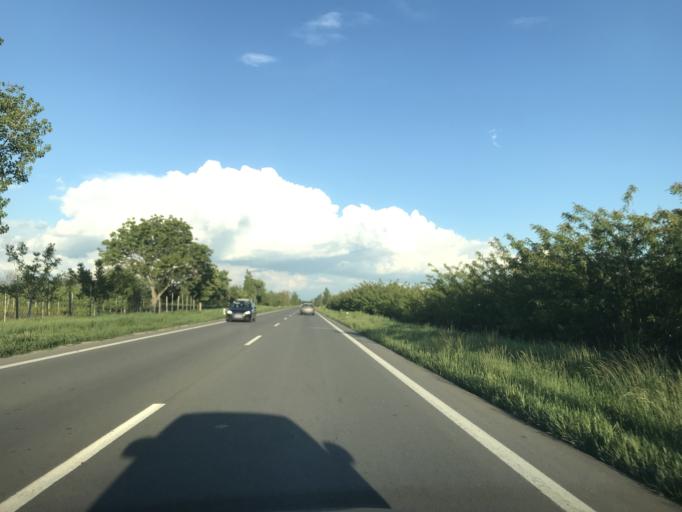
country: RS
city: Aradac
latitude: 45.3864
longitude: 20.3183
